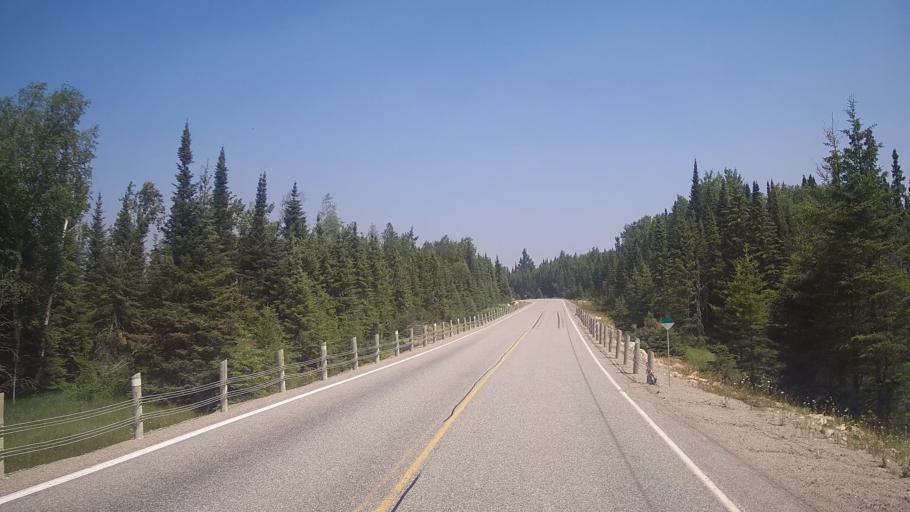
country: CA
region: Ontario
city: Timmins
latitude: 48.0532
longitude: -81.5824
